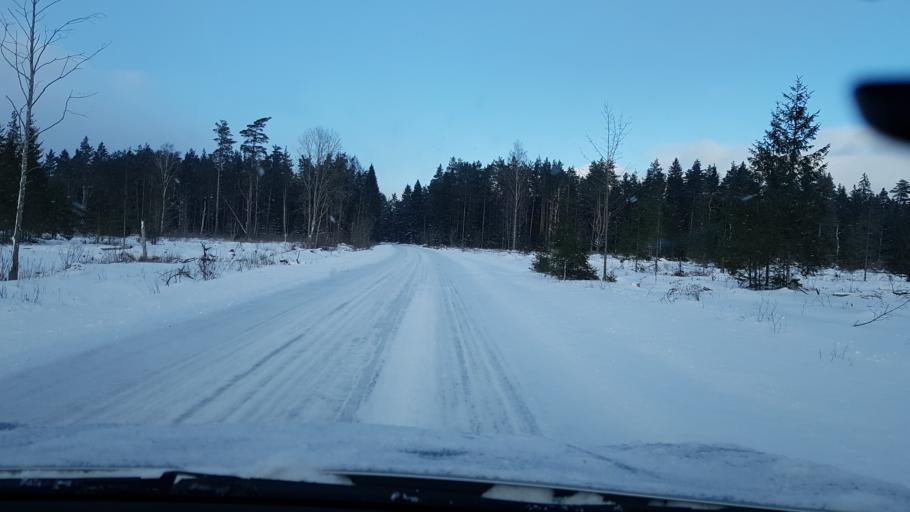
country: EE
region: Harju
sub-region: Nissi vald
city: Turba
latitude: 59.2068
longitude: 24.1407
